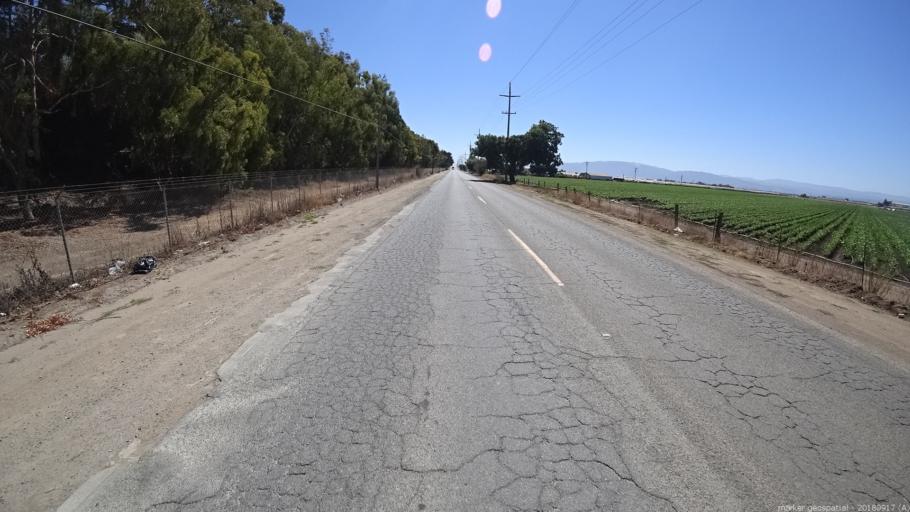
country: US
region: California
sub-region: Monterey County
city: Prunedale
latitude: 36.7535
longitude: -121.6089
